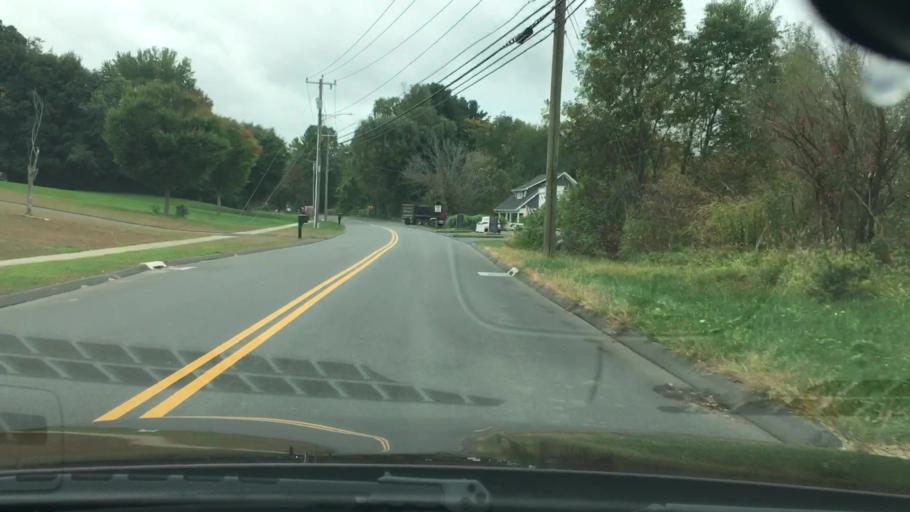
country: US
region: Connecticut
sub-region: Hartford County
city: Hazardville
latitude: 42.0004
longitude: -72.5147
